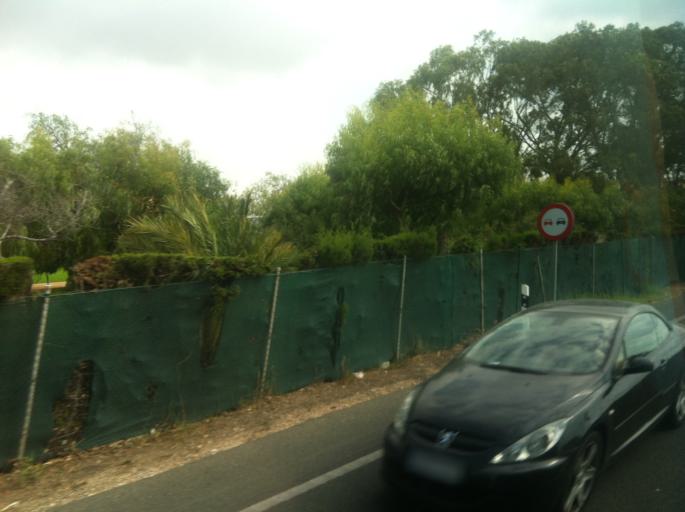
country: ES
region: Valencia
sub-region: Provincia de Alicante
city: Santa Pola
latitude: 38.1901
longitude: -0.5966
